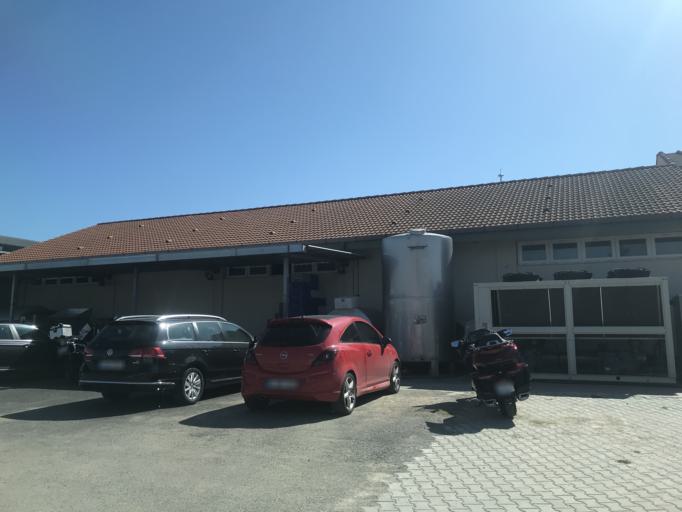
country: TR
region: Tekirdag
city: Kumbag
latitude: 40.9280
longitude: 27.4360
